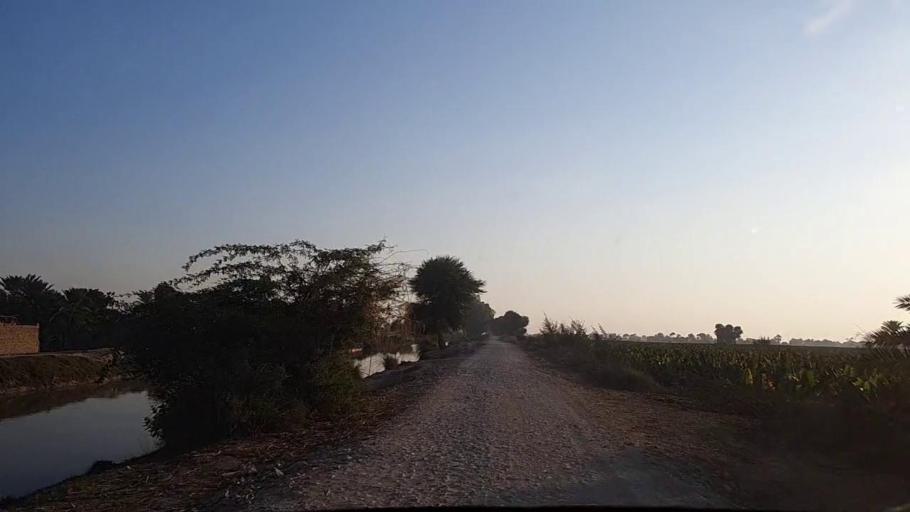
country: PK
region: Sindh
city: Sobhadero
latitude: 27.3863
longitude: 68.3825
